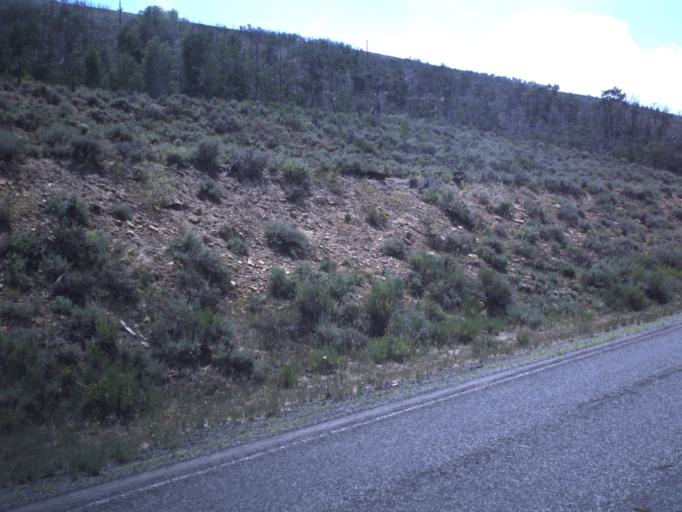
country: US
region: Utah
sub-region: Carbon County
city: Helper
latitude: 39.7372
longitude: -111.1530
